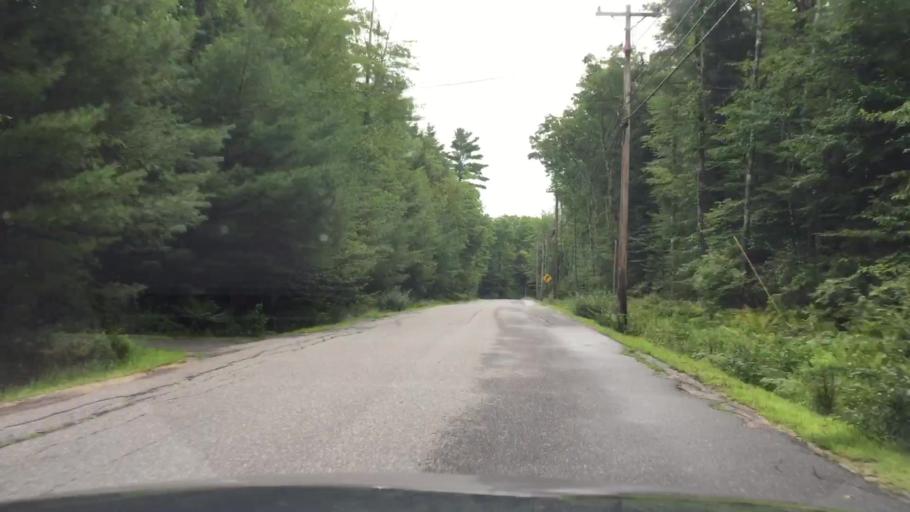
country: US
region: New Hampshire
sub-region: Carroll County
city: Center Harbor
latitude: 43.7289
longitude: -71.4878
